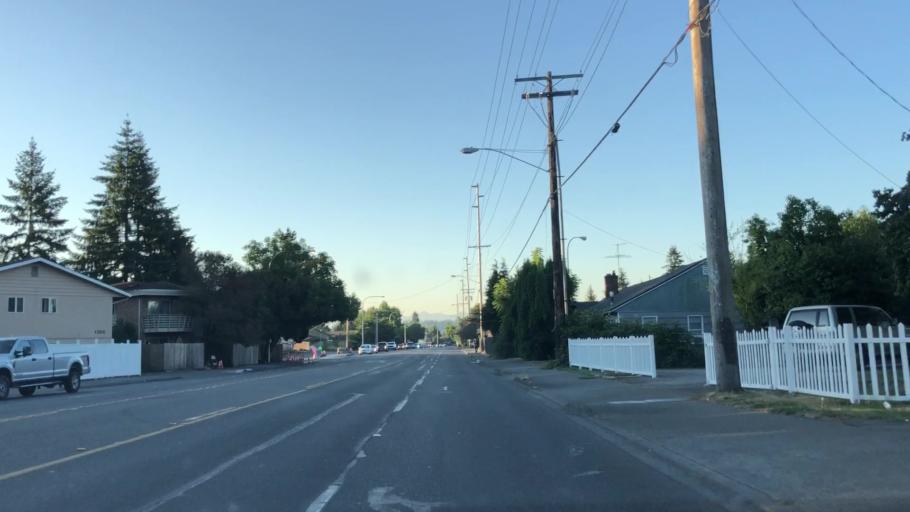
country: US
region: Washington
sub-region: King County
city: Auburn
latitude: 47.3191
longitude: -122.2192
